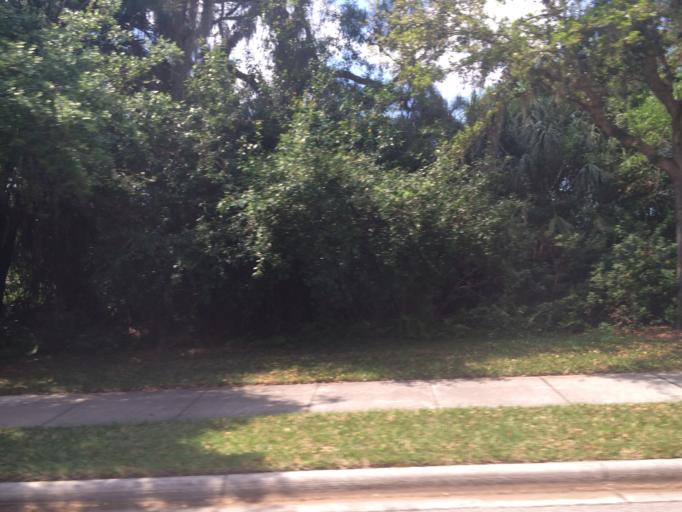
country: US
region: Florida
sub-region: Manatee County
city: Ellenton
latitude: 27.4889
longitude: -82.4130
